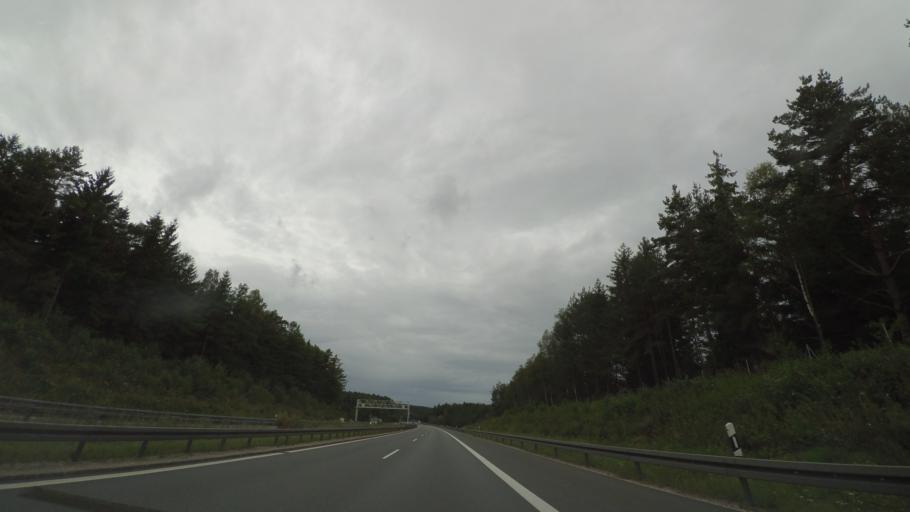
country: DE
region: Bavaria
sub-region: Upper Palatinate
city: Kummersbruck
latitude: 49.3982
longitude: 11.8526
